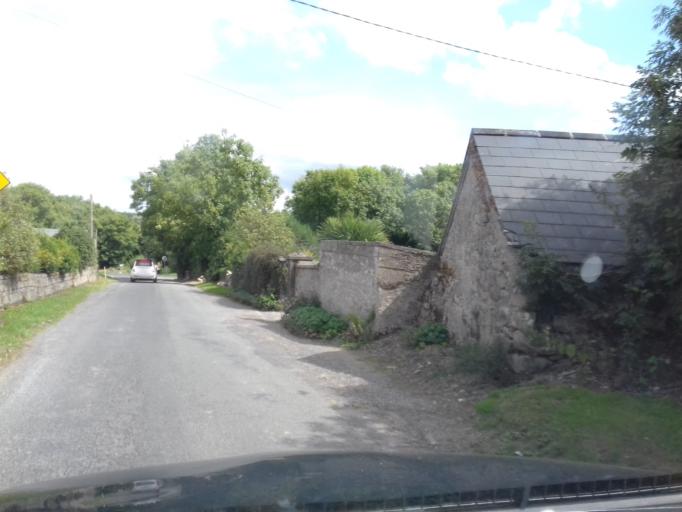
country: IE
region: Leinster
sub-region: Kilkenny
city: Graiguenamanagh
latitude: 52.5961
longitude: -6.9574
